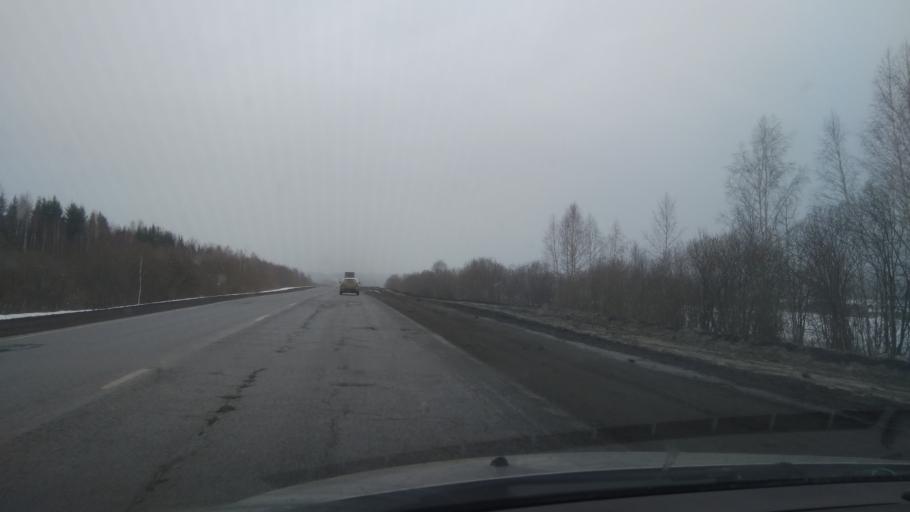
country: RU
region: Perm
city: Orda
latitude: 57.2832
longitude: 56.9993
